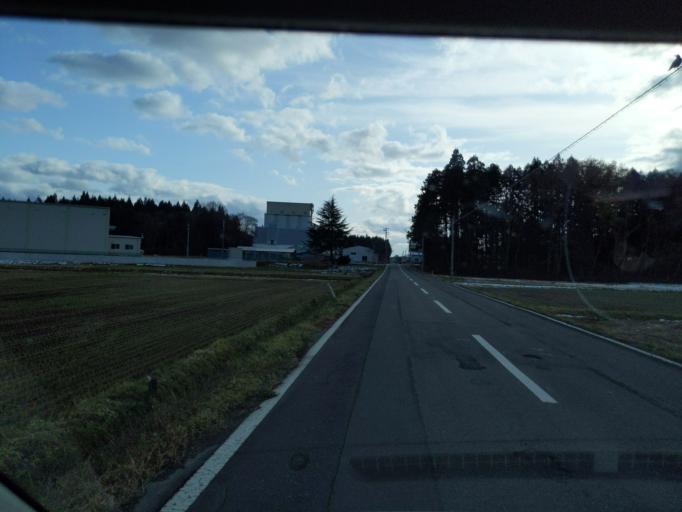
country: JP
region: Iwate
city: Mizusawa
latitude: 39.1071
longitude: 141.0818
